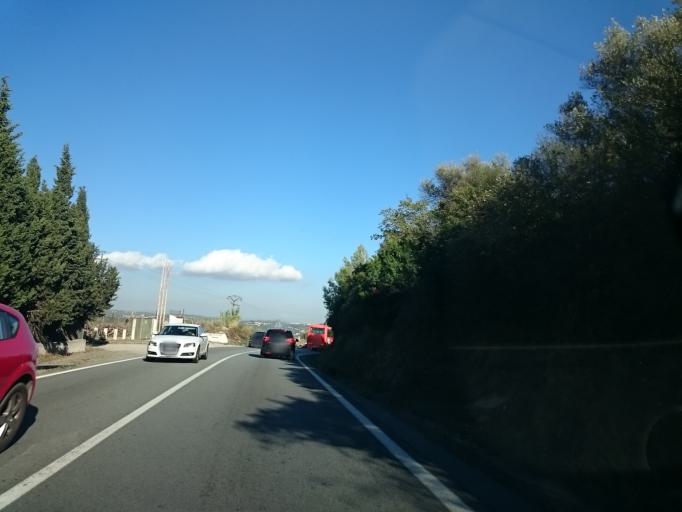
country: ES
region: Catalonia
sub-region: Provincia de Barcelona
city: Castellvi de Rosanes
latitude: 41.4786
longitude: 1.8936
